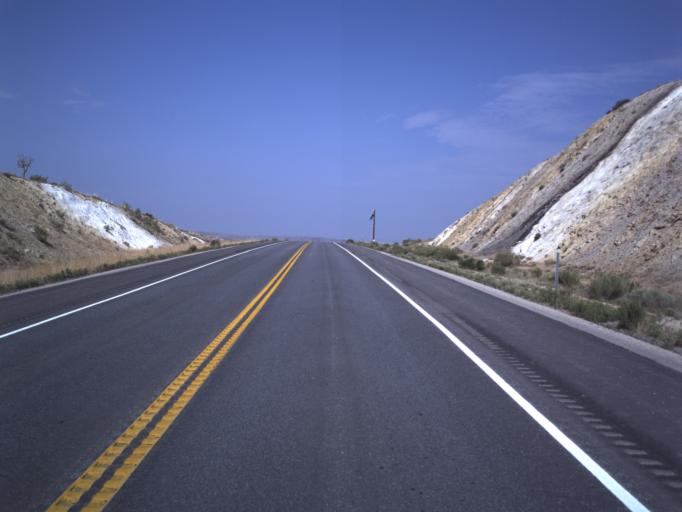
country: US
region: Colorado
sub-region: Rio Blanco County
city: Rangely
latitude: 40.2797
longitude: -109.0654
